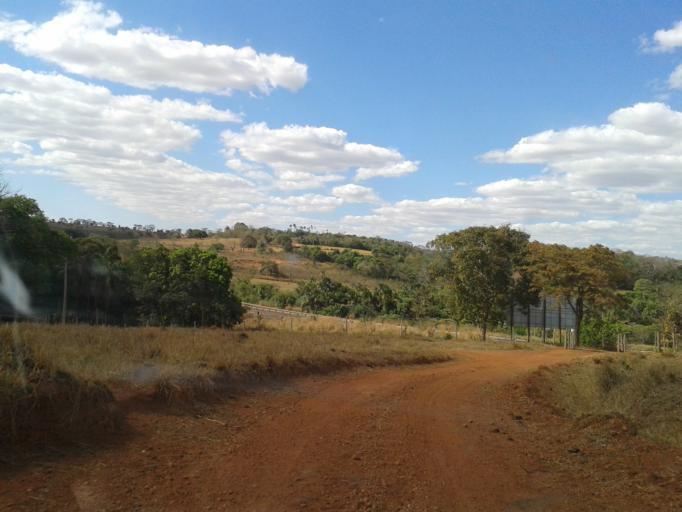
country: BR
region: Minas Gerais
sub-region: Monte Alegre De Minas
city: Monte Alegre de Minas
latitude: -18.7933
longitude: -49.0854
